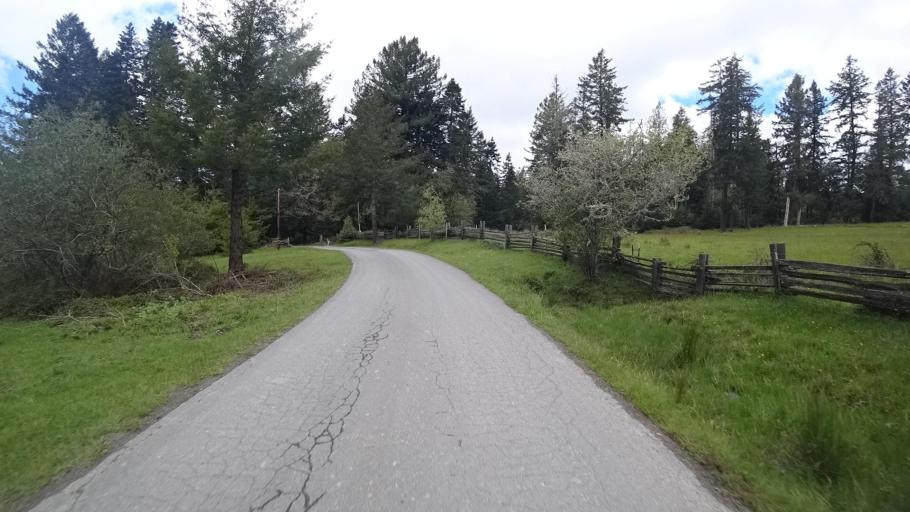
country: US
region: California
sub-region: Humboldt County
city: Blue Lake
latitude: 40.9089
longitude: -123.9705
